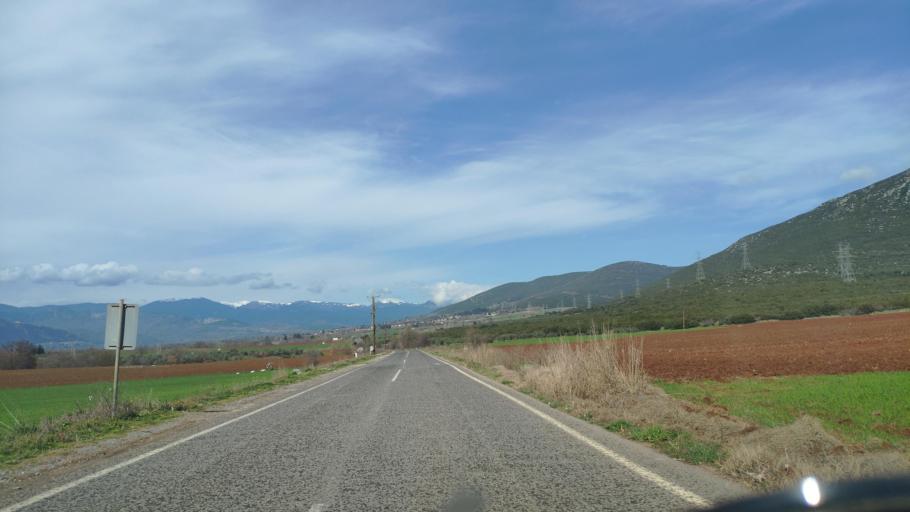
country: GR
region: Central Greece
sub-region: Nomos Fthiotidos
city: Amfikleia
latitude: 38.6975
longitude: 22.5202
